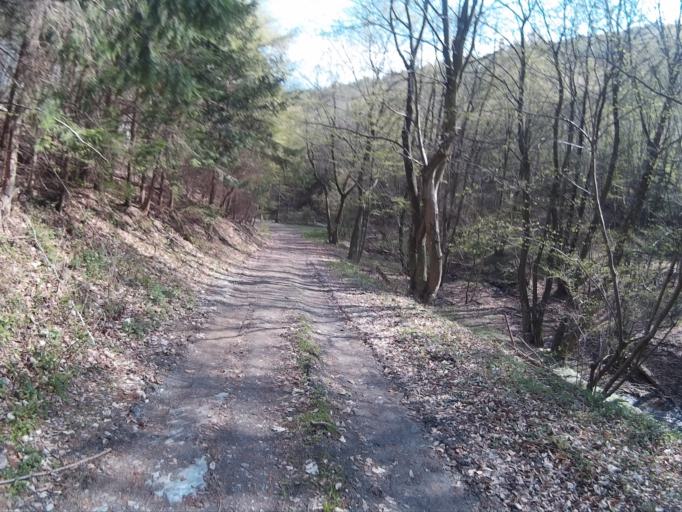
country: AT
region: Burgenland
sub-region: Politischer Bezirk Oberwart
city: Rechnitz
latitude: 47.3411
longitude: 16.4473
